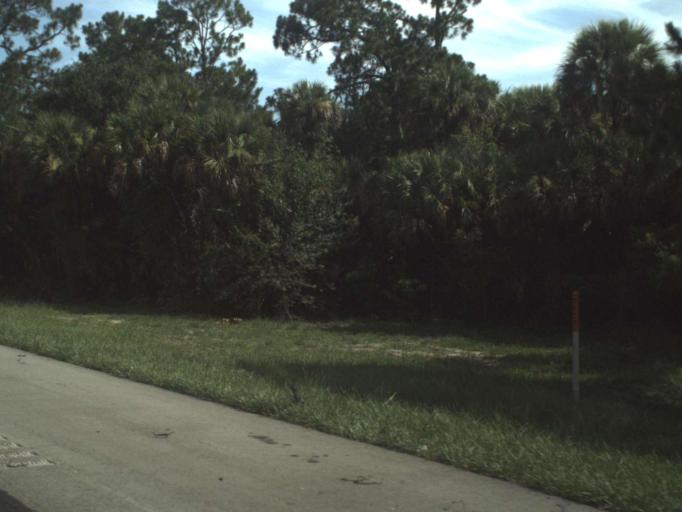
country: US
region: Florida
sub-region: Indian River County
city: West Vero Corridor
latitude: 27.5587
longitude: -80.4808
